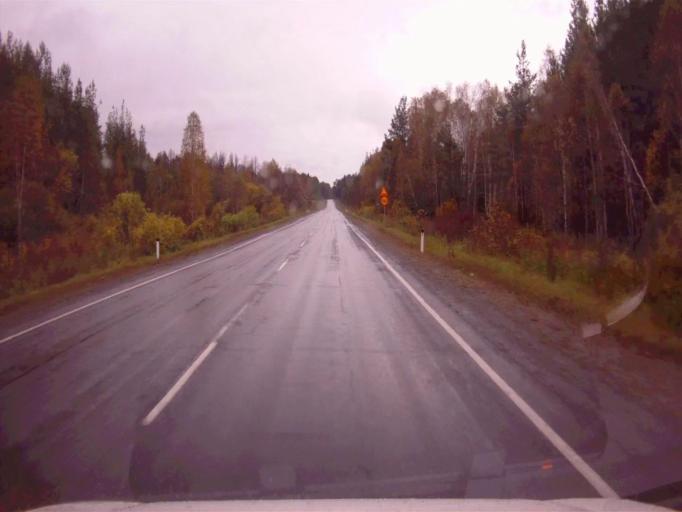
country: RU
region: Chelyabinsk
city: Verkhniy Ufaley
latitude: 56.0166
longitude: 60.3087
